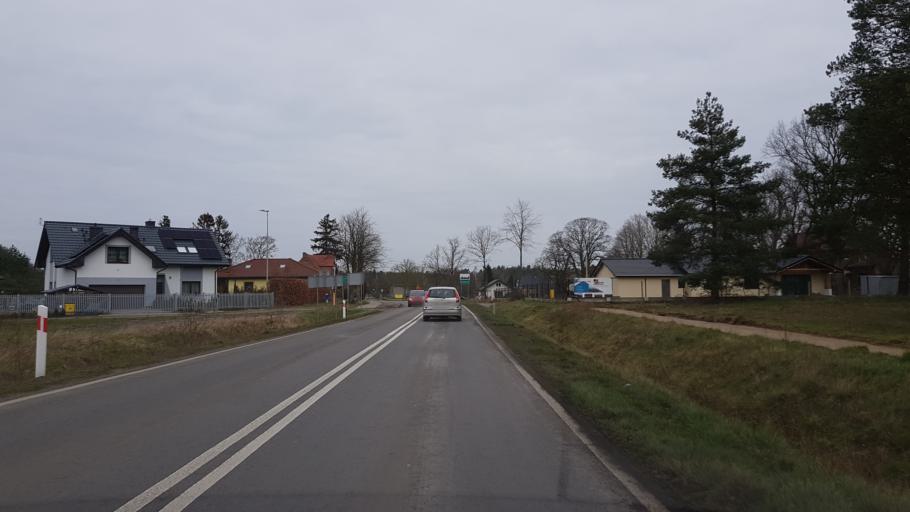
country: PL
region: West Pomeranian Voivodeship
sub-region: Powiat policki
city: Police
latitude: 53.6233
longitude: 14.5038
